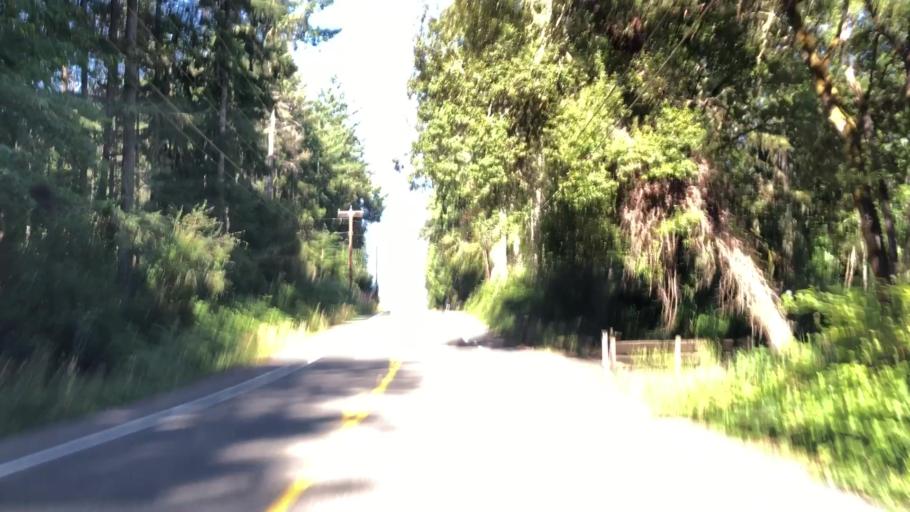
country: US
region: Washington
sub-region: Kitsap County
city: Kingston
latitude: 47.7730
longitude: -122.5104
